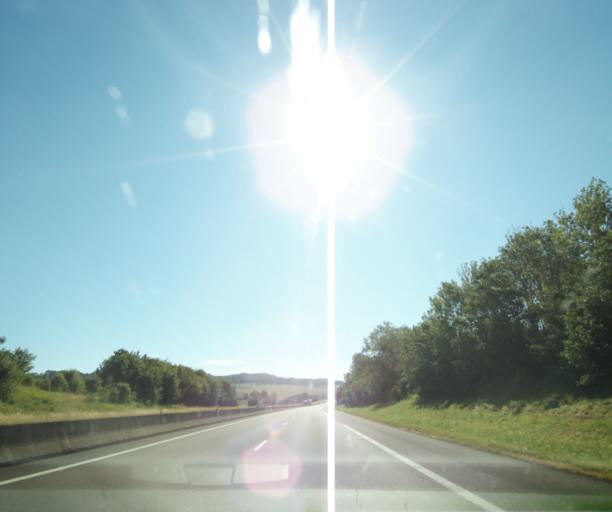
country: FR
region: Champagne-Ardenne
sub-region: Departement de la Haute-Marne
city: Nogent-le-Bas
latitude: 47.9583
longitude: 5.3986
